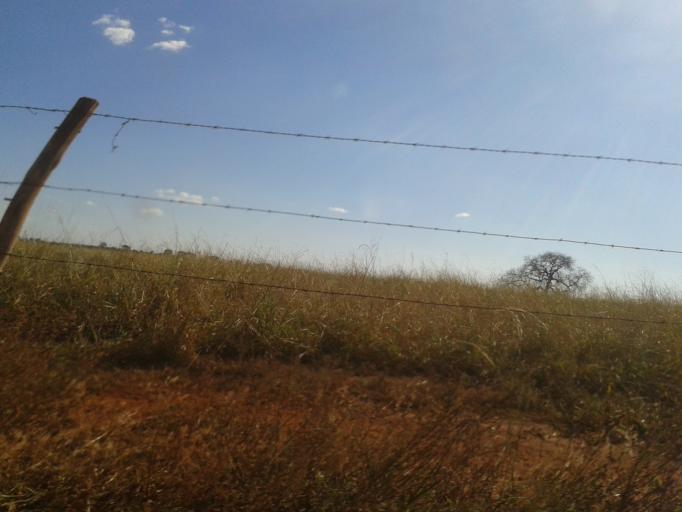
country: BR
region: Minas Gerais
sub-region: Centralina
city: Centralina
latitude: -18.7486
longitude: -49.1876
